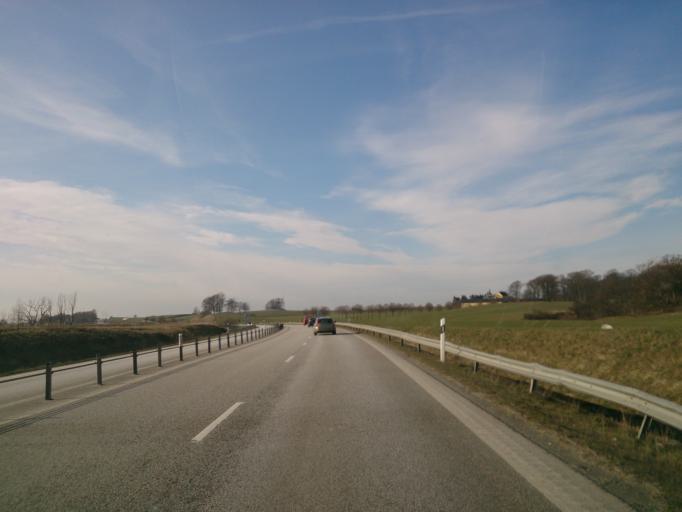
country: SE
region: Skane
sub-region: Ystads Kommun
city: Ystad
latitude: 55.4444
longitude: 13.7791
